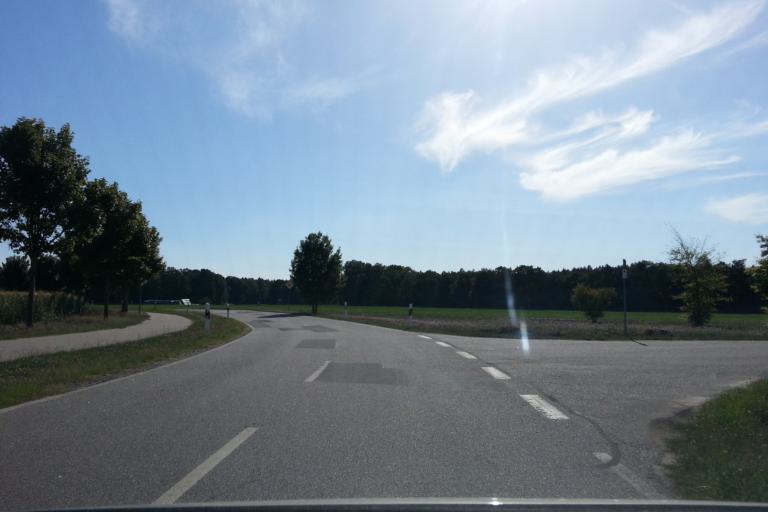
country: DE
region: Mecklenburg-Vorpommern
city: Eggesin
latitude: 53.6783
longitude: 14.0358
